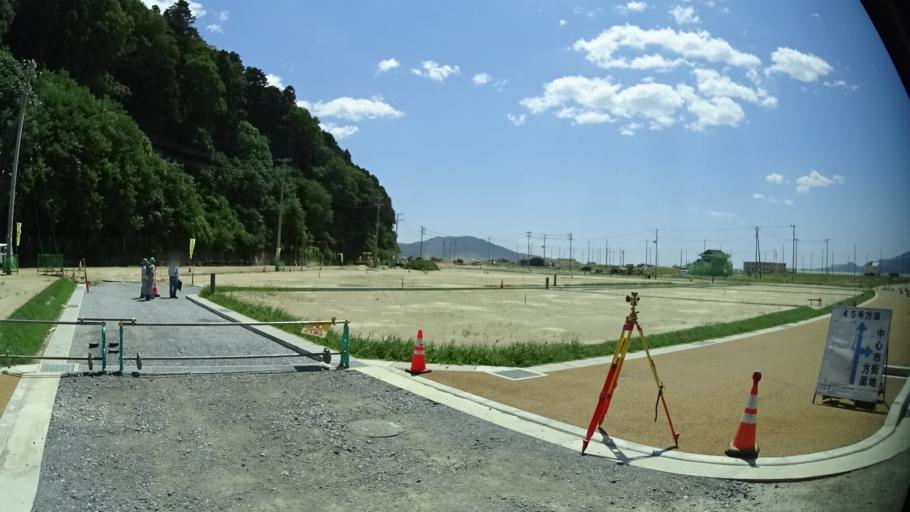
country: JP
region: Iwate
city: Ofunato
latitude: 39.0171
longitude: 141.6339
